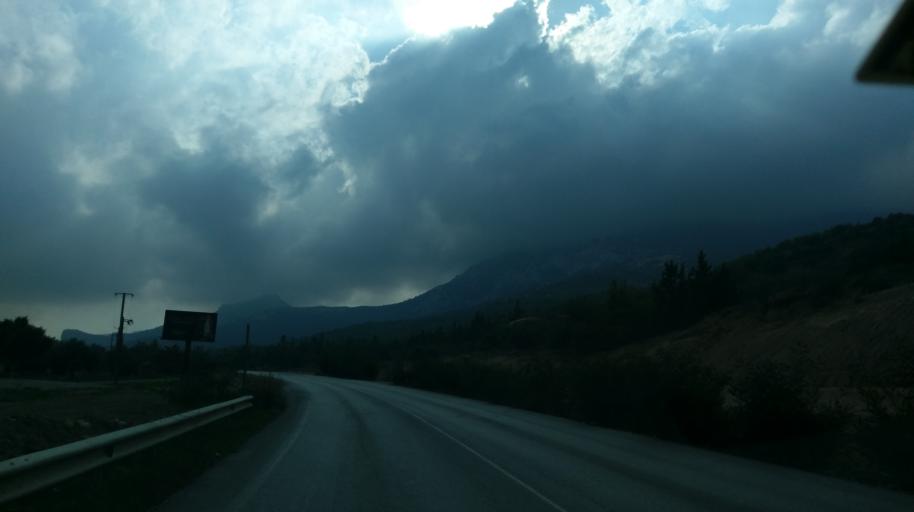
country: CY
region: Keryneia
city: Kyrenia
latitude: 35.3059
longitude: 33.4240
